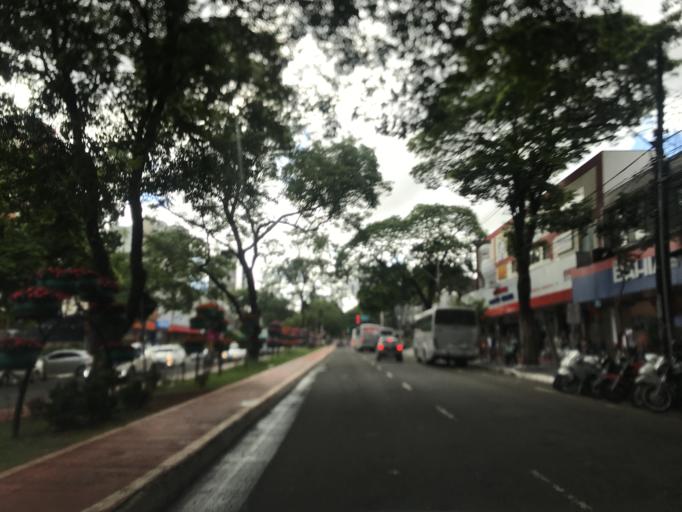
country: BR
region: Parana
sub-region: Maringa
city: Maringa
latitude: -23.4209
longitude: -51.9350
